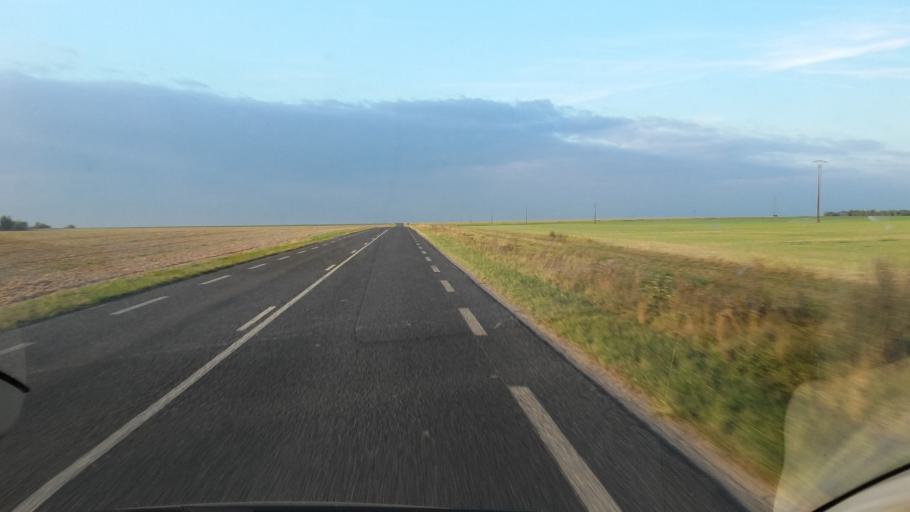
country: FR
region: Champagne-Ardenne
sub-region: Departement de la Marne
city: Fere-Champenoise
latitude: 48.7787
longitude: 3.9940
